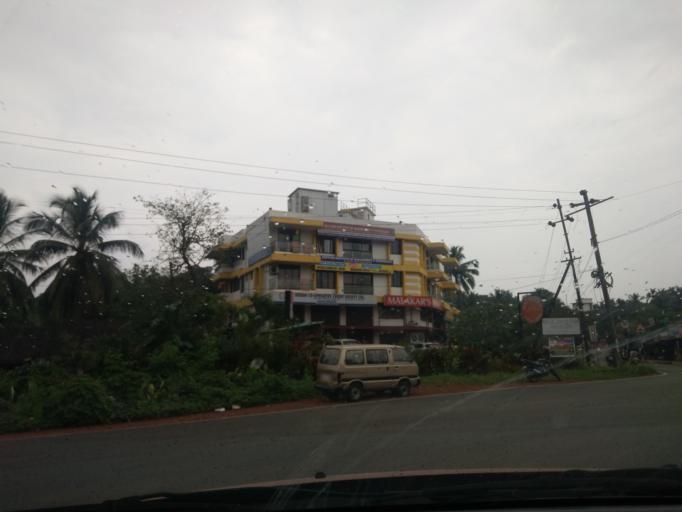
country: IN
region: Goa
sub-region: South Goa
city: Sancoale
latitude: 15.3561
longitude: 73.9281
